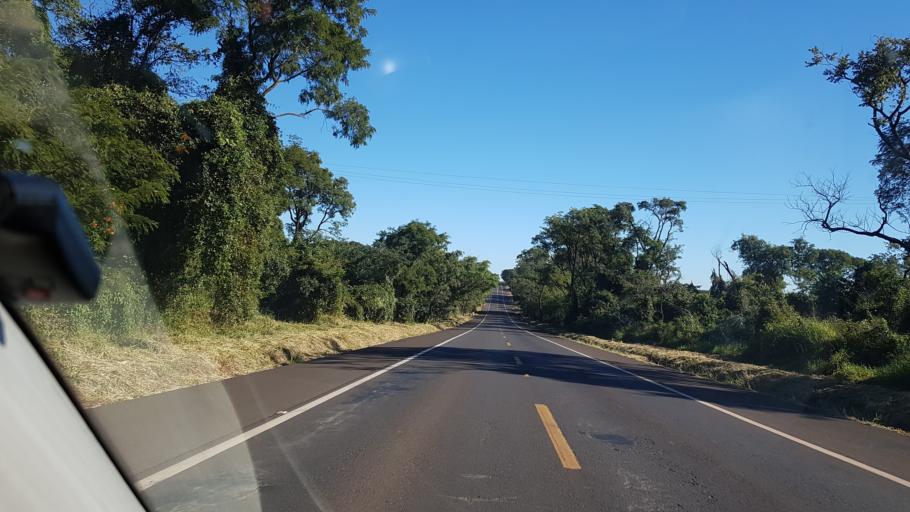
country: BR
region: Sao Paulo
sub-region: Assis
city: Assis
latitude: -22.5813
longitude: -50.5056
